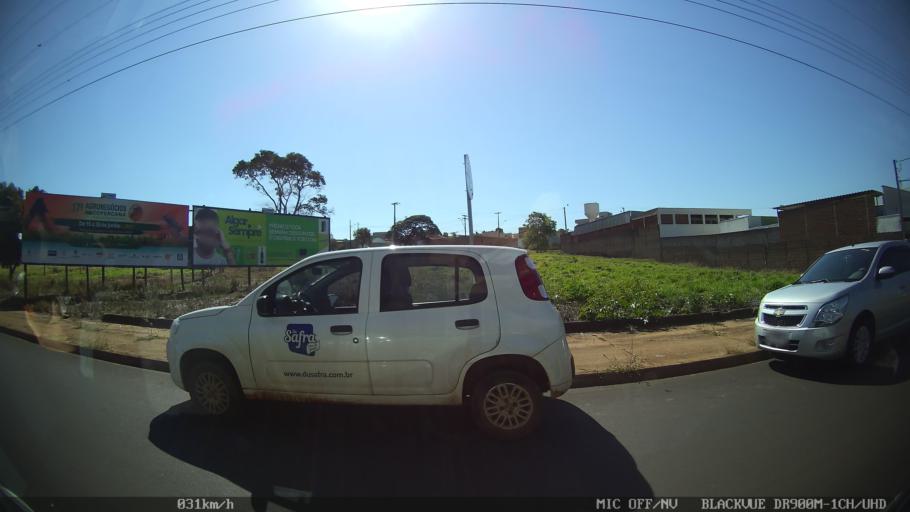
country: BR
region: Sao Paulo
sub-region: Batatais
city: Batatais
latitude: -20.8837
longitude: -47.5864
